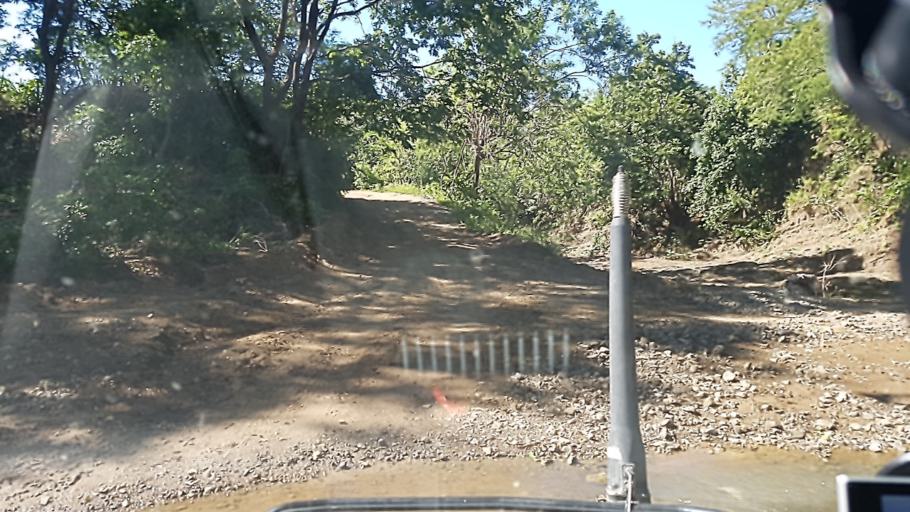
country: NI
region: Rivas
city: Tola
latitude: 11.5415
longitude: -86.1067
